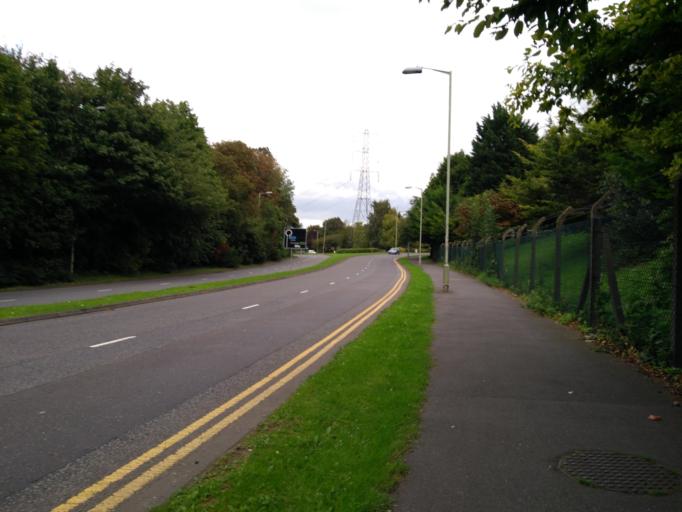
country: GB
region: England
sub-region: Central Bedfordshire
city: Houghton Regis
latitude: 51.8970
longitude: -0.5123
